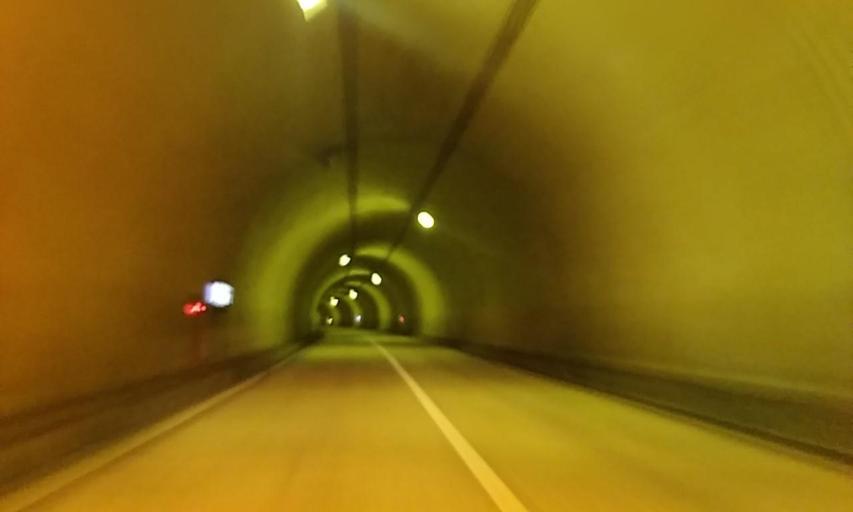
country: JP
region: Wakayama
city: Shingu
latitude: 33.8964
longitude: 135.8795
